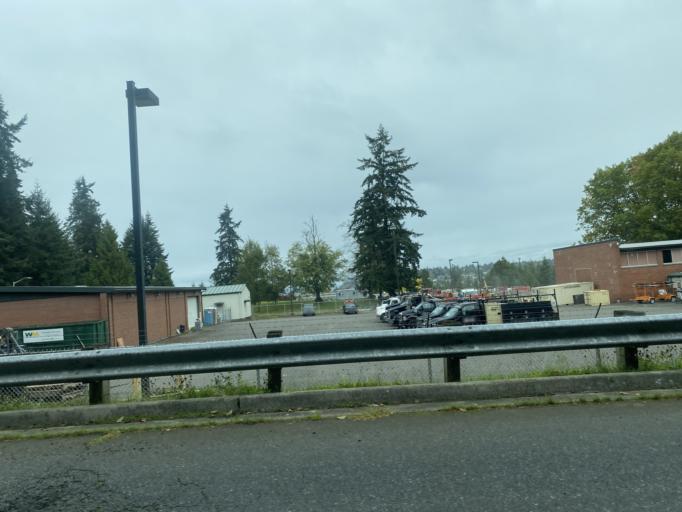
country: US
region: Washington
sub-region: King County
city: Seattle
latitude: 47.6609
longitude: -122.4051
